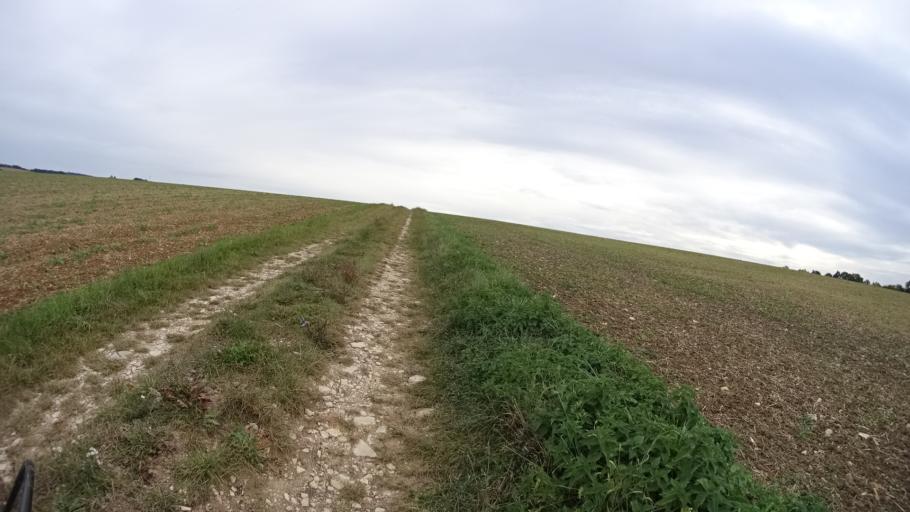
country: DE
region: Bavaria
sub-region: Upper Bavaria
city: Hitzhofen
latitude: 48.8645
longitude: 11.3371
